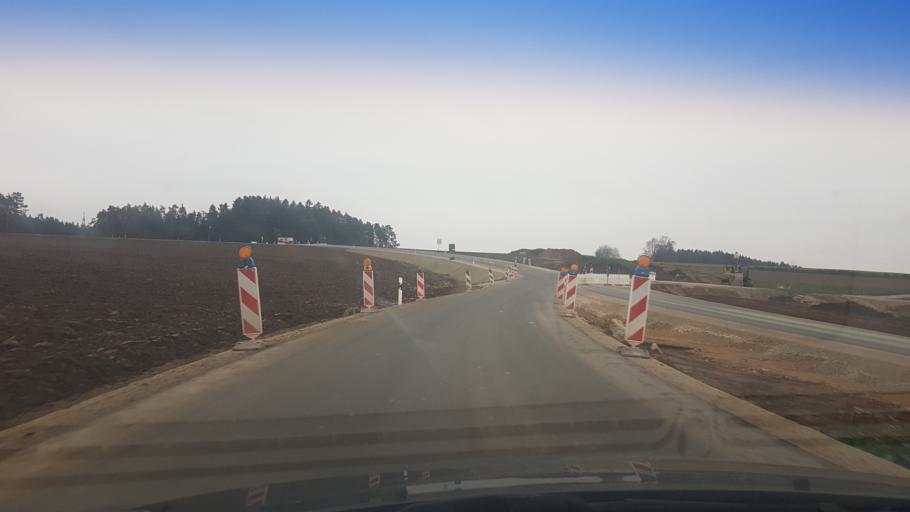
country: DE
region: Bavaria
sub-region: Upper Franconia
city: Wonsees
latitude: 50.0265
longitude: 11.2672
